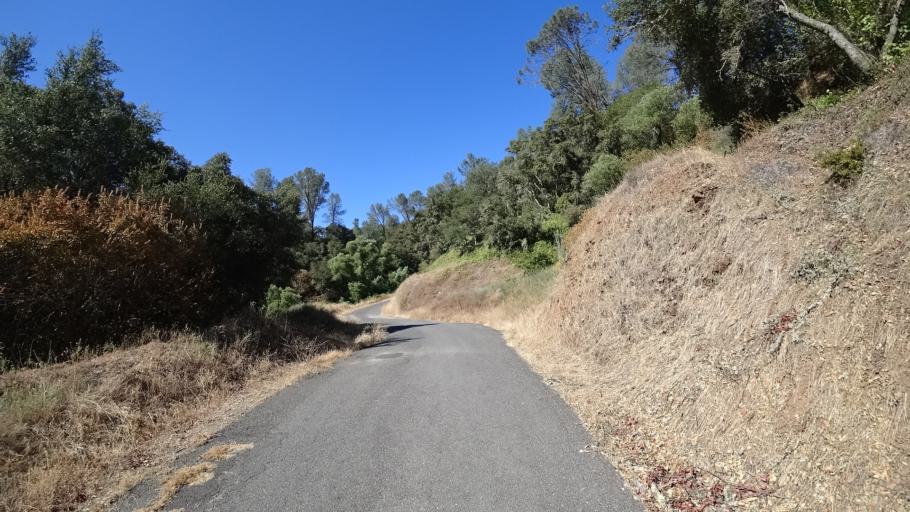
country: US
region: California
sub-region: Amador County
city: Jackson
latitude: 38.2716
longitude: -120.7598
